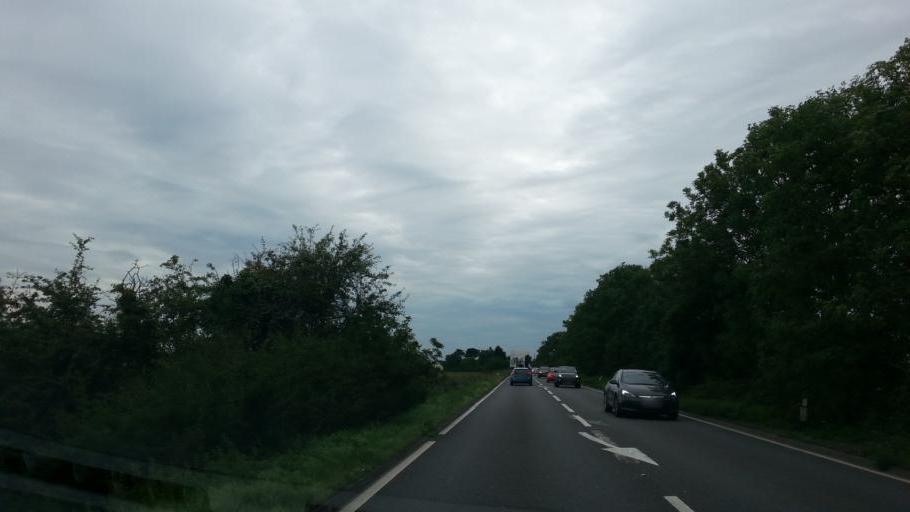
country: GB
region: England
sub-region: Cambridgeshire
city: March
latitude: 52.6181
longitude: 0.0796
